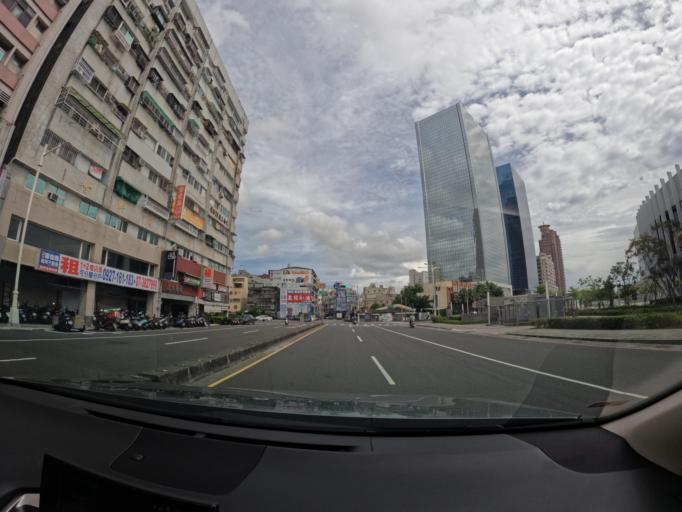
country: TW
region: Kaohsiung
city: Kaohsiung
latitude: 22.6178
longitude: 120.2937
